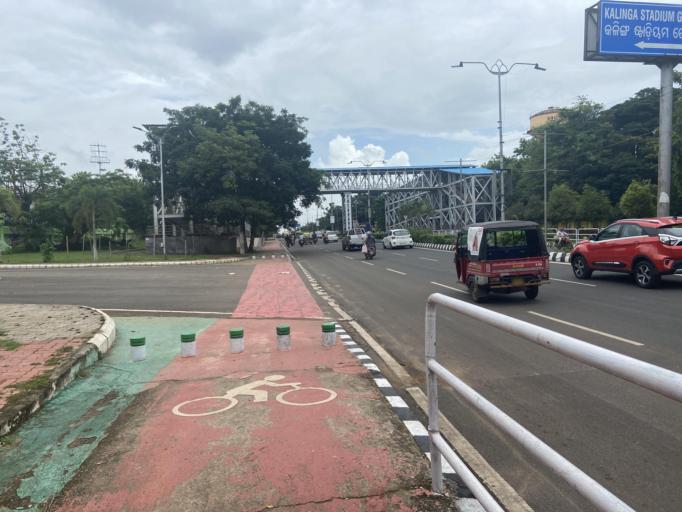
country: IN
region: Odisha
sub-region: Khordha
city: Bhubaneshwar
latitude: 20.2889
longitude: 85.8261
